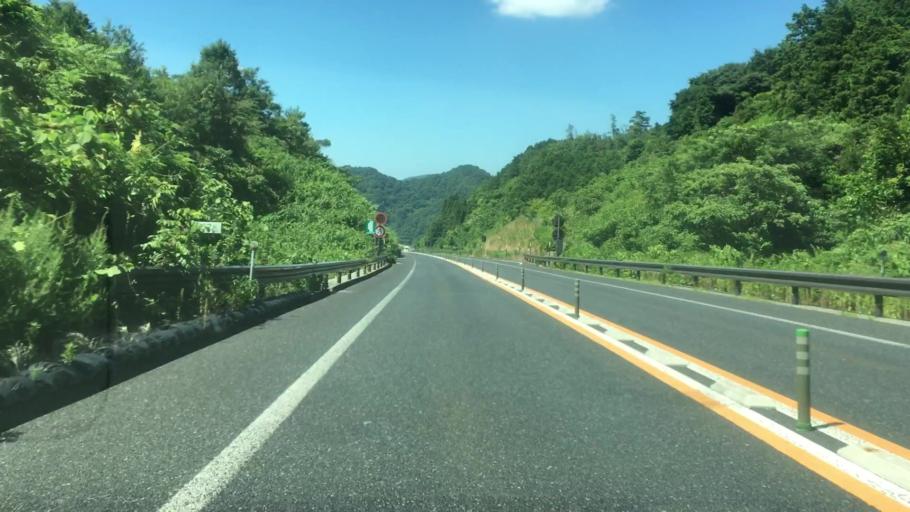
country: JP
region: Tottori
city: Tottori
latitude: 35.3662
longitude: 134.2022
